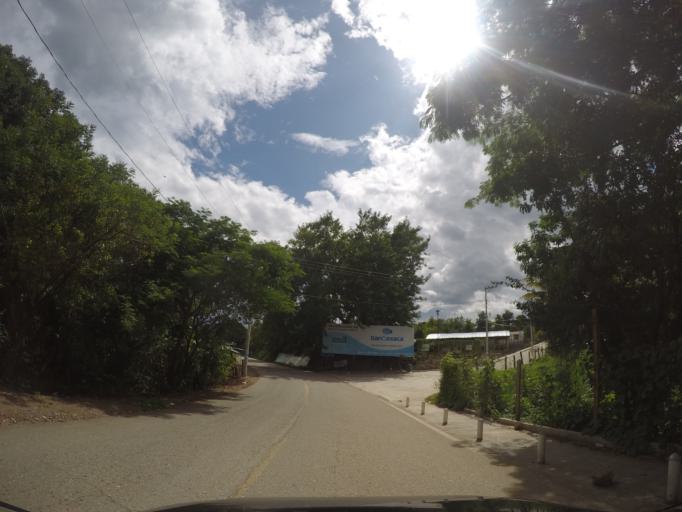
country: MX
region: Oaxaca
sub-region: San Jeronimo Coatlan
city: San Cristobal Honduras
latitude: 16.4338
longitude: -97.0627
